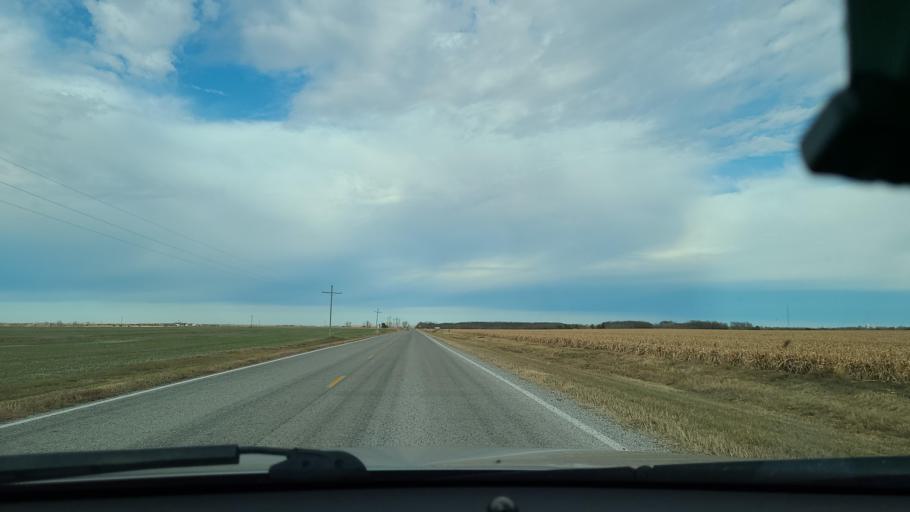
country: US
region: Kansas
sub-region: McPherson County
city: Inman
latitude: 38.3707
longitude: -97.9245
